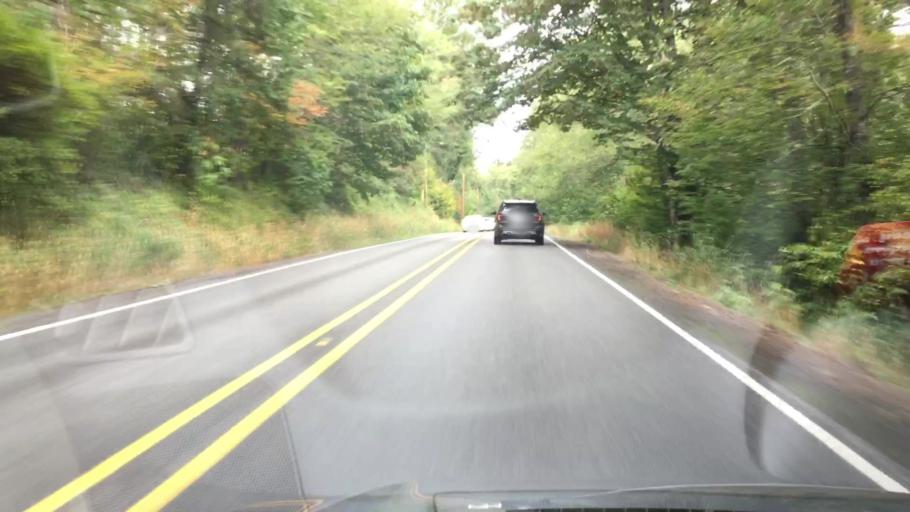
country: US
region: Washington
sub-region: Pierce County
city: Eatonville
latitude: 46.8467
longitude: -122.2564
